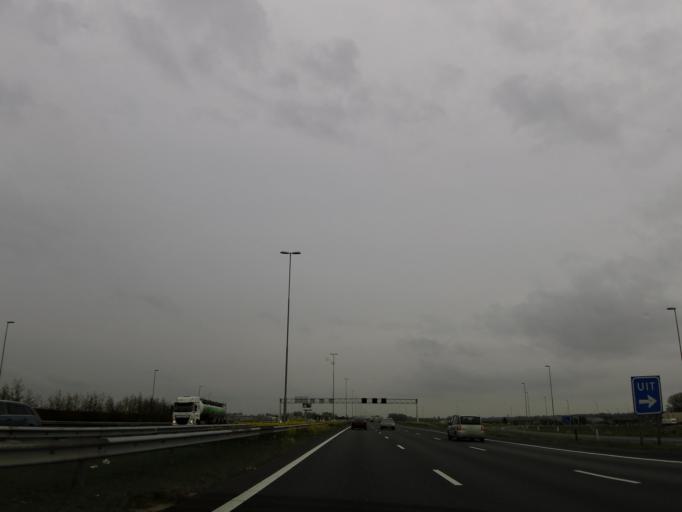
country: NL
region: Gelderland
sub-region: Gemeente Maasdriel
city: Hedel
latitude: 51.7606
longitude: 5.2799
